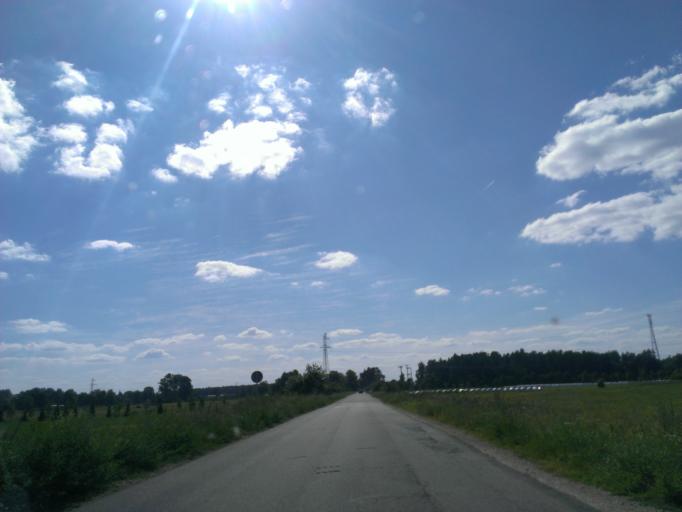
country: LV
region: Adazi
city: Adazi
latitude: 57.0923
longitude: 24.3043
